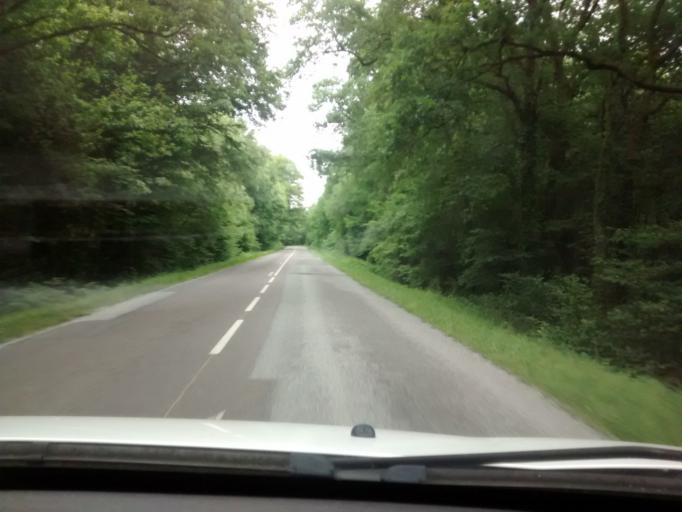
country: FR
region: Brittany
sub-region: Departement d'Ille-et-Vilaine
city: Servon-sur-Vilaine
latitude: 48.1424
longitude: -1.4491
